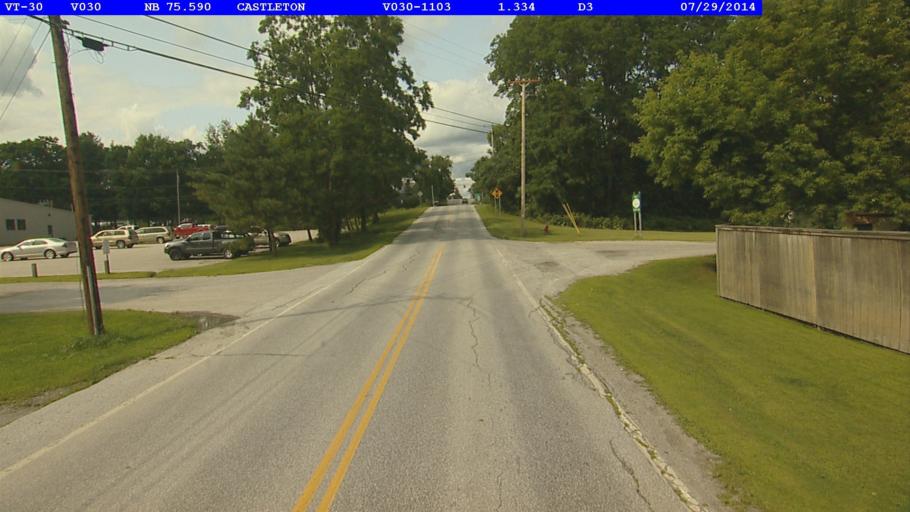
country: US
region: Vermont
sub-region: Rutland County
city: Castleton
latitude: 43.6059
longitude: -73.2090
